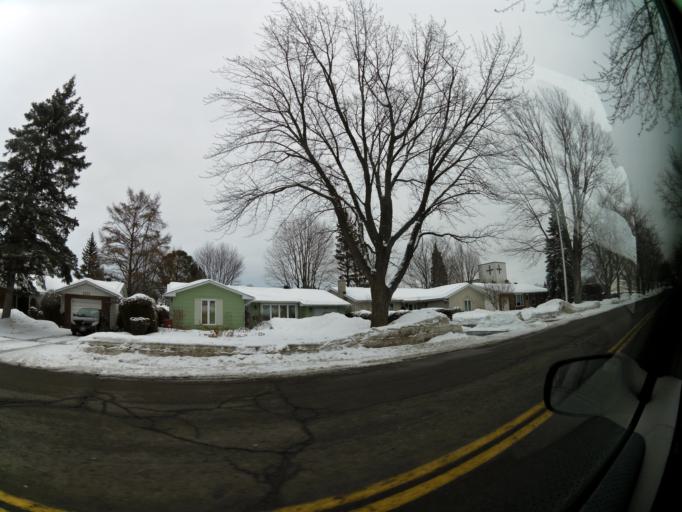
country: CA
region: Quebec
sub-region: Outaouais
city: Gatineau
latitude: 45.4592
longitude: -75.6017
